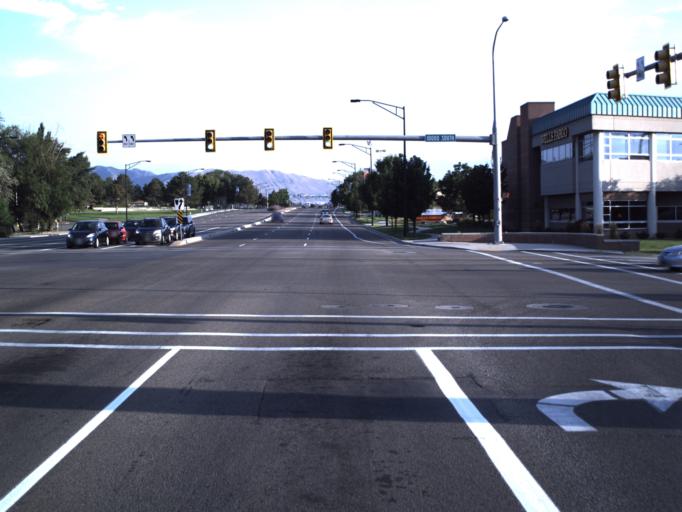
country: US
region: Utah
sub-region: Salt Lake County
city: Sandy City
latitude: 40.5700
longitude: -111.8909
